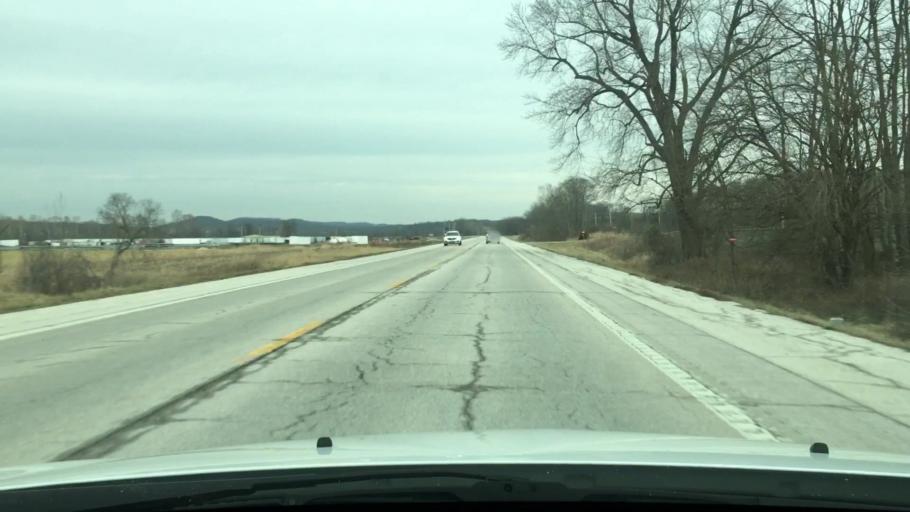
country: US
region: Missouri
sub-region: Pike County
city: Bowling Green
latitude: 39.3814
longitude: -91.1357
